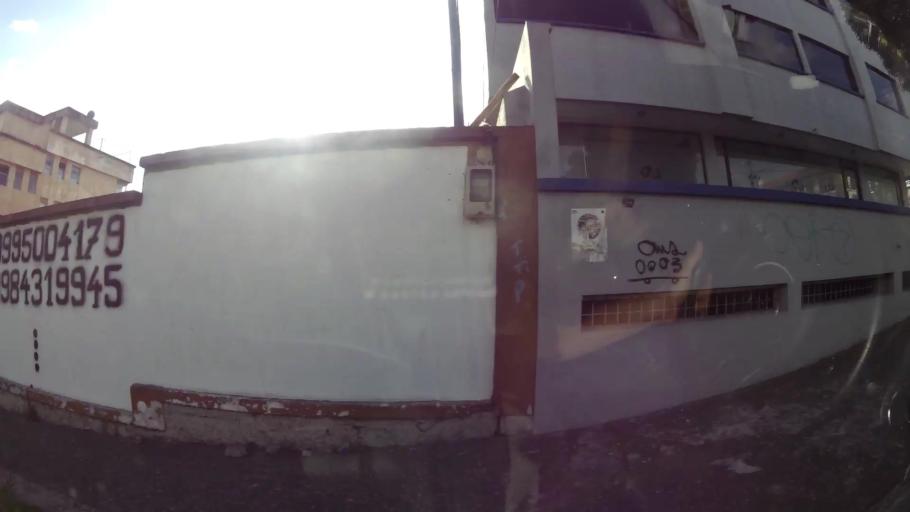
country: EC
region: Pichincha
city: Quito
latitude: -0.2069
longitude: -78.4840
